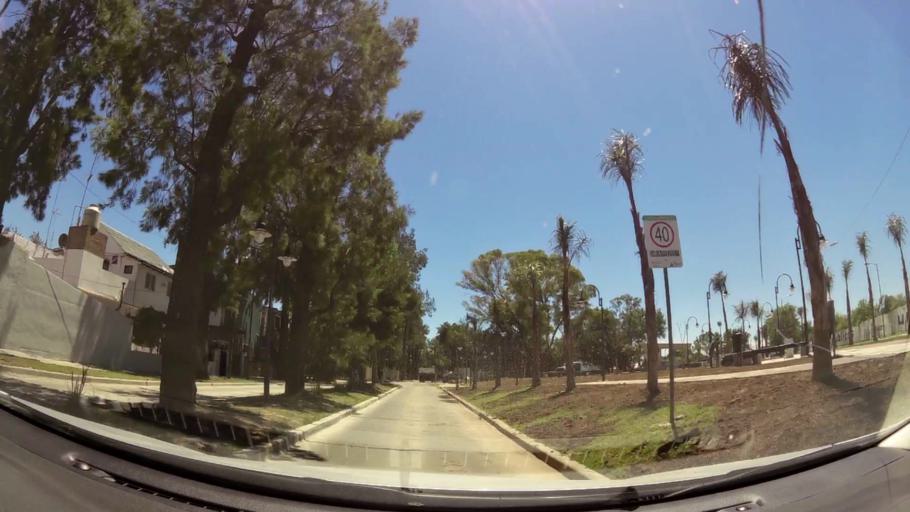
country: AR
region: Buenos Aires
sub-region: Partido de Tigre
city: Tigre
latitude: -34.4570
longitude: -58.5554
